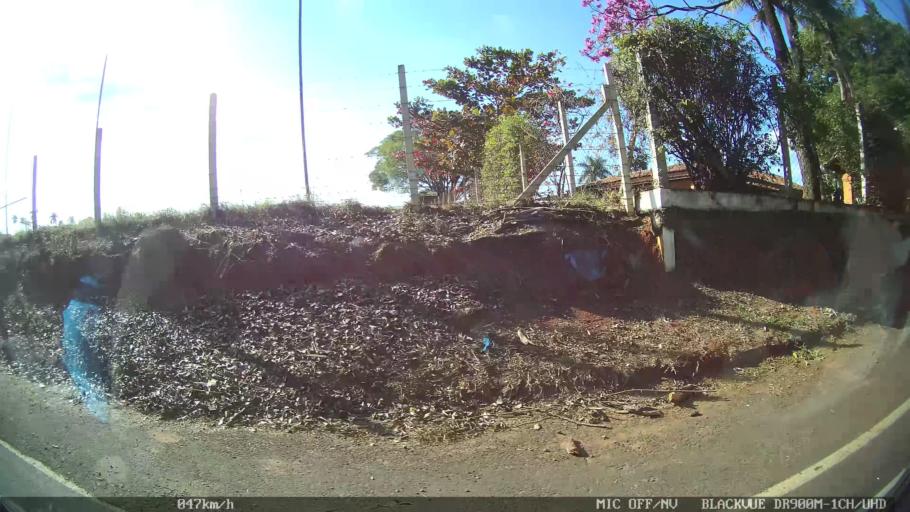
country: BR
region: Sao Paulo
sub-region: Nova Odessa
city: Nova Odessa
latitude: -22.8121
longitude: -47.3293
